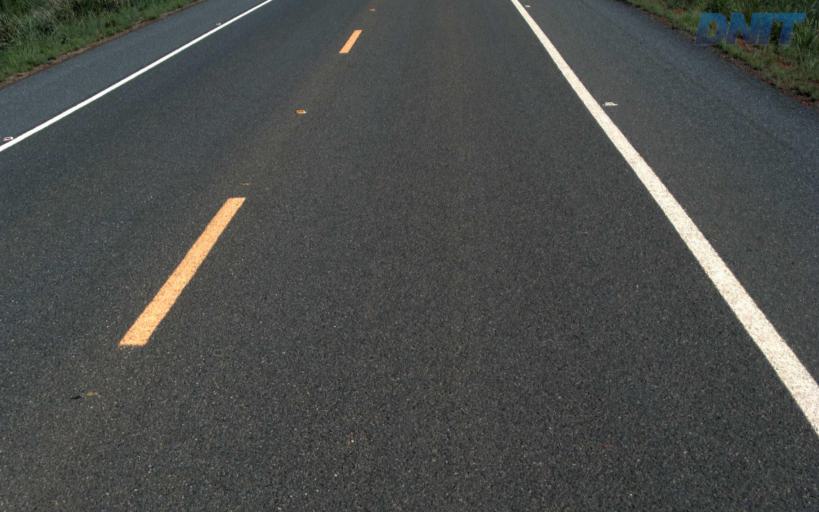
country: BR
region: Goias
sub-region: Sao Miguel Do Araguaia
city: Sao Miguel do Araguaia
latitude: -13.4236
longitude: -50.1284
